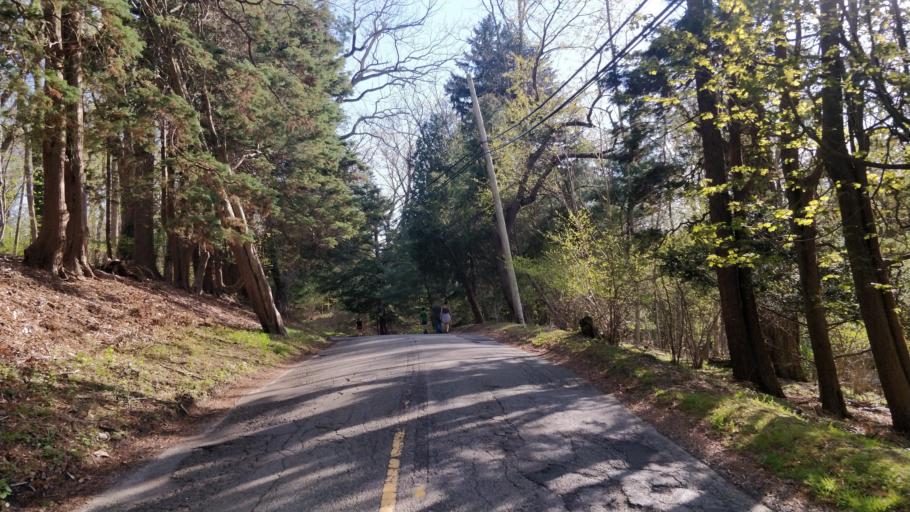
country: US
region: New York
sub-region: Suffolk County
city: Head of the Harbor
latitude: 40.9023
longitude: -73.1674
